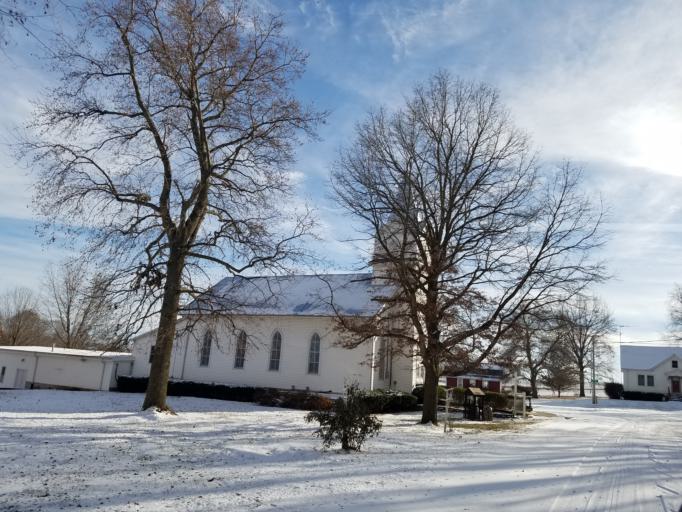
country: US
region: Missouri
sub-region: Carroll County
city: Carrollton
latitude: 39.2052
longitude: -93.4410
